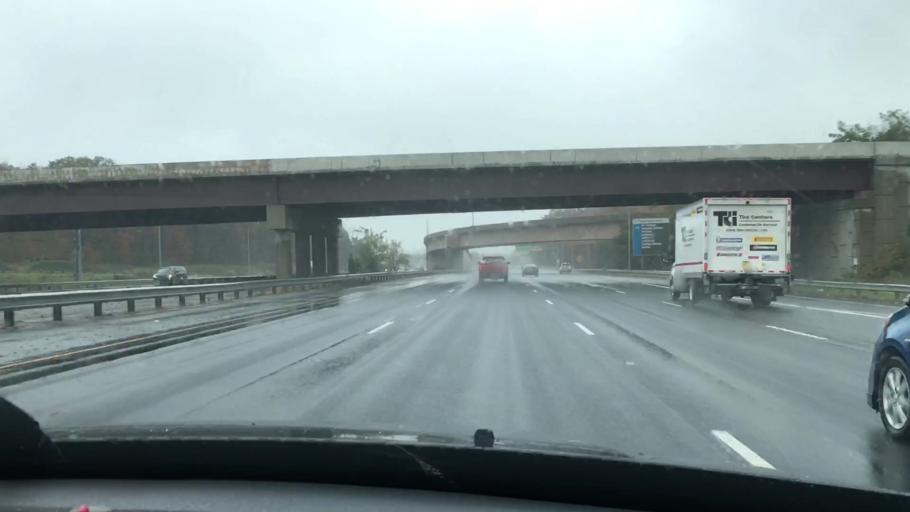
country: US
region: Virginia
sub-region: Loudoun County
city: Oak Grove
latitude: 38.9708
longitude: -77.4294
